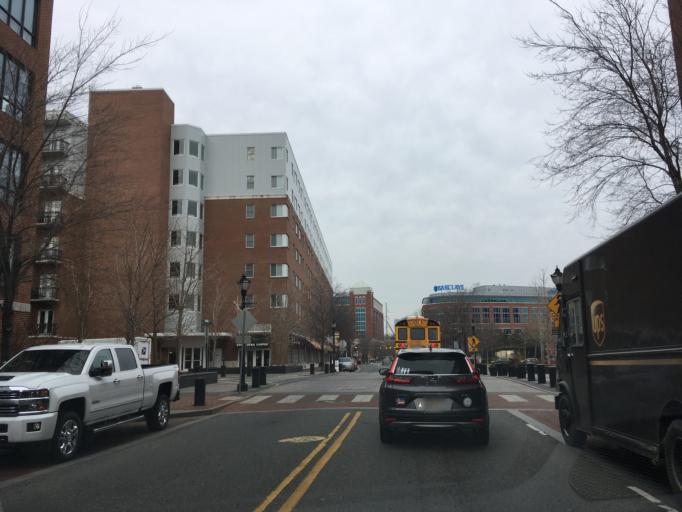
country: US
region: Delaware
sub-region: New Castle County
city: Wilmington
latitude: 39.7357
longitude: -75.5604
